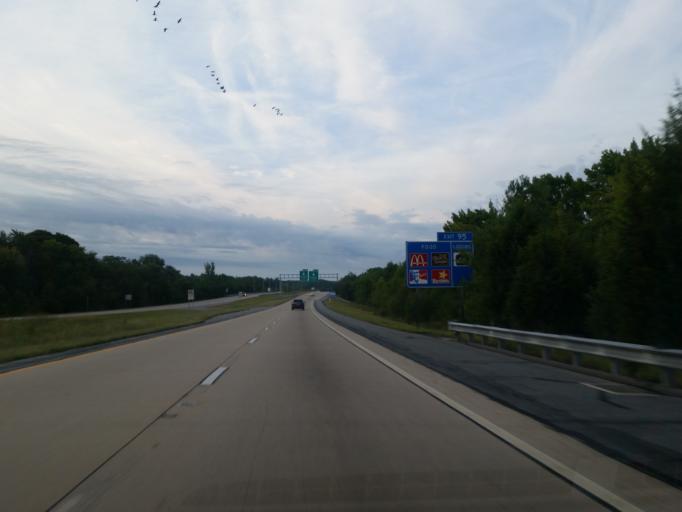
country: US
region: Delaware
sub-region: Kent County
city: Dover
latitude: 39.1625
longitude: -75.4929
